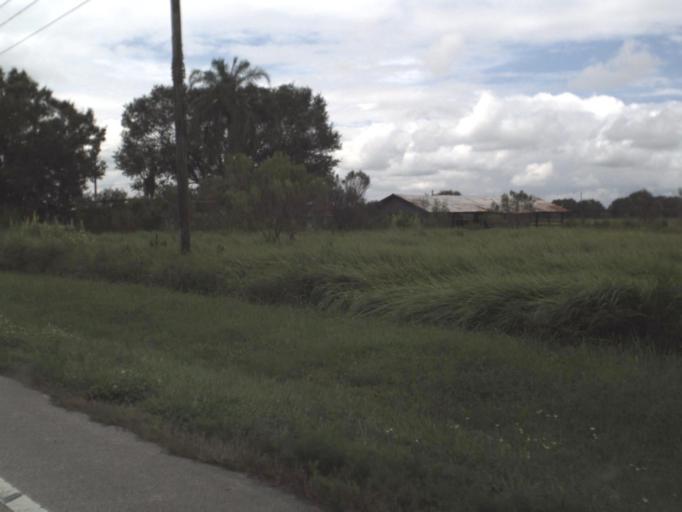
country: US
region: Florida
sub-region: Hardee County
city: Bowling Green
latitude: 27.5948
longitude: -81.9033
